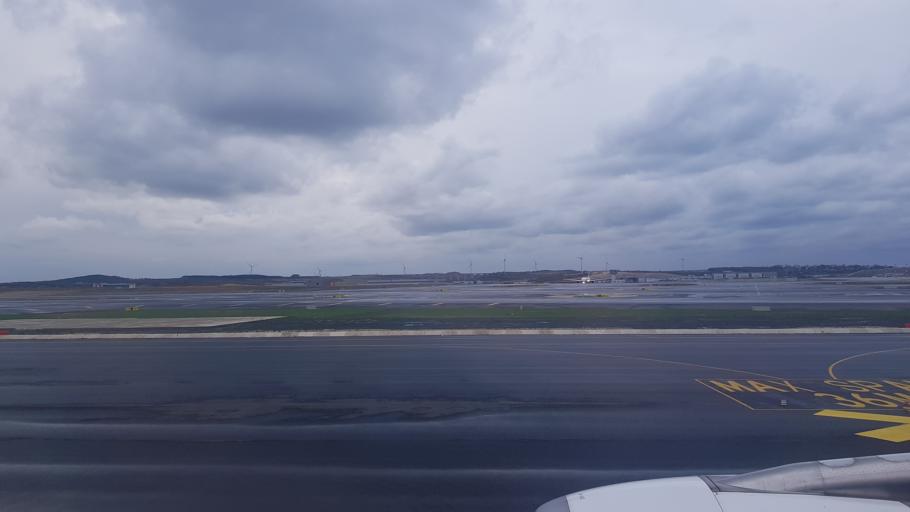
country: TR
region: Istanbul
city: Durusu
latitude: 41.2640
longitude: 28.7345
